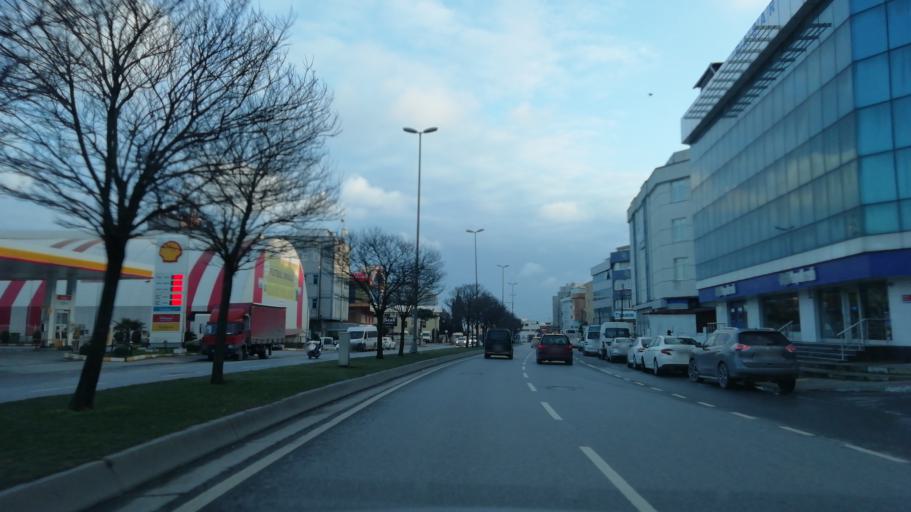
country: TR
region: Istanbul
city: Yakuplu
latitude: 40.9996
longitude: 28.7130
